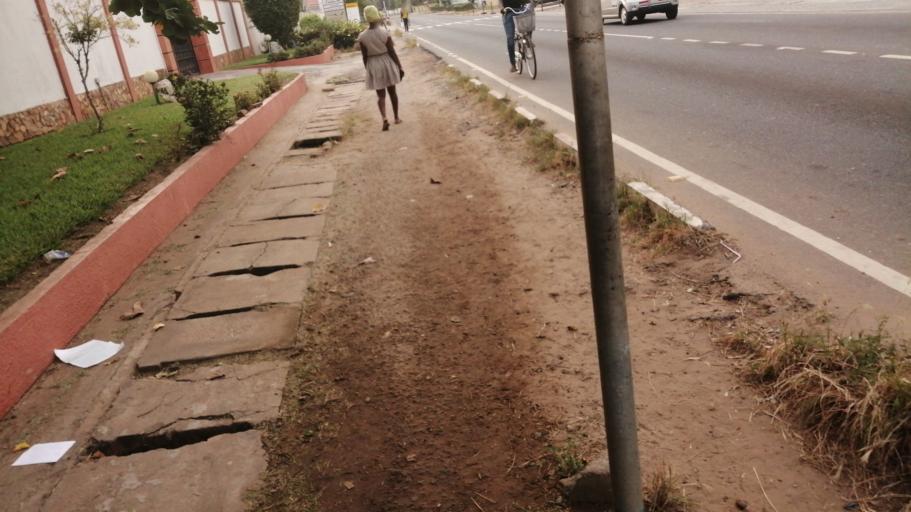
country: GH
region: Greater Accra
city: Medina Estates
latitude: 5.6193
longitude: -0.1783
